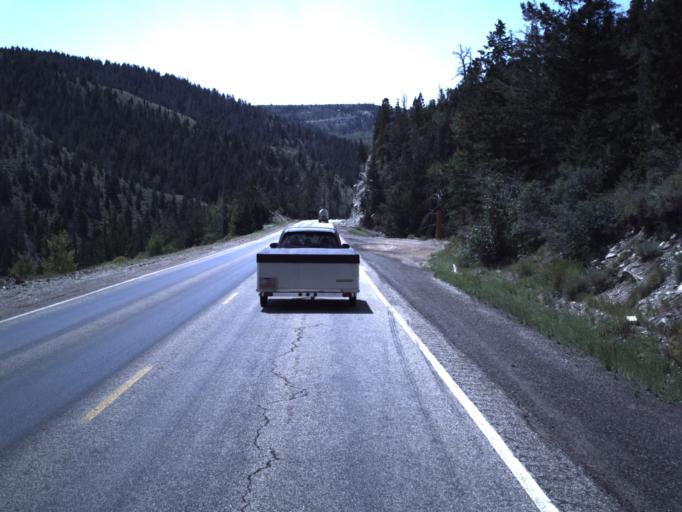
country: US
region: Utah
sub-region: Carbon County
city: Helper
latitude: 39.8602
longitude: -110.7656
